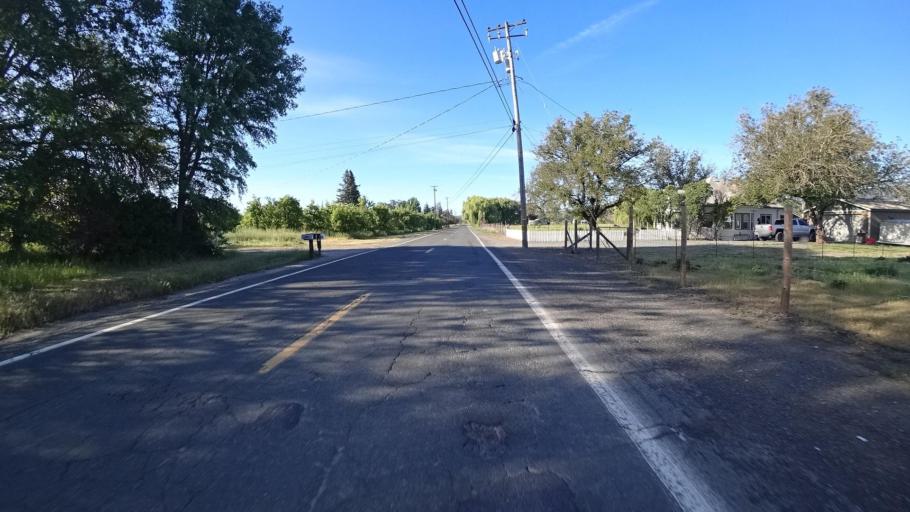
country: US
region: California
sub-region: Lake County
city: North Lakeport
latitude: 39.0752
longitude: -122.9498
